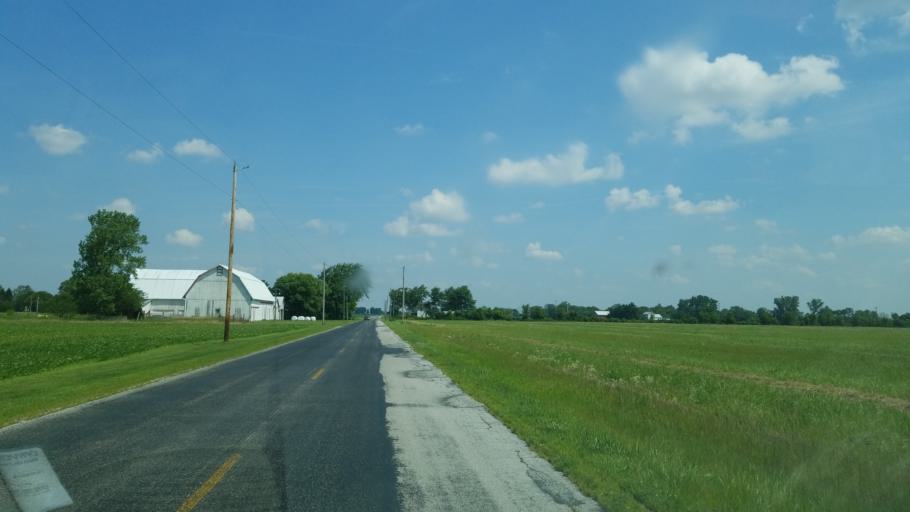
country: US
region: Ohio
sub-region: Seneca County
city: Fostoria
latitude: 41.2503
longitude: -83.5353
